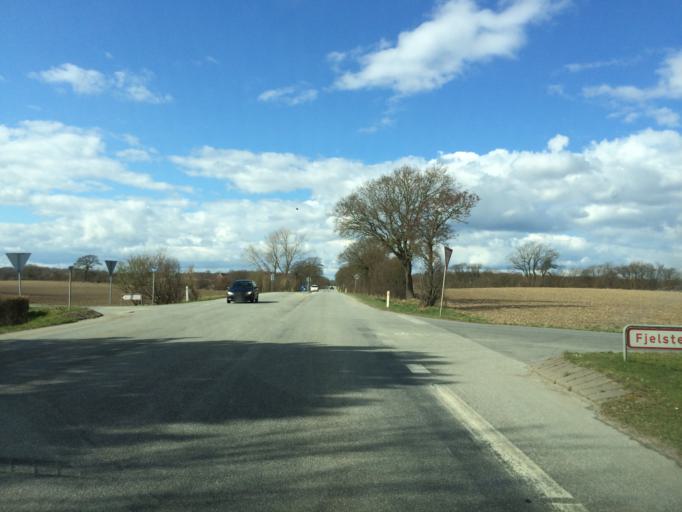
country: DK
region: South Denmark
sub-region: Middelfart Kommune
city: Brenderup
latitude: 55.4391
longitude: 9.9973
